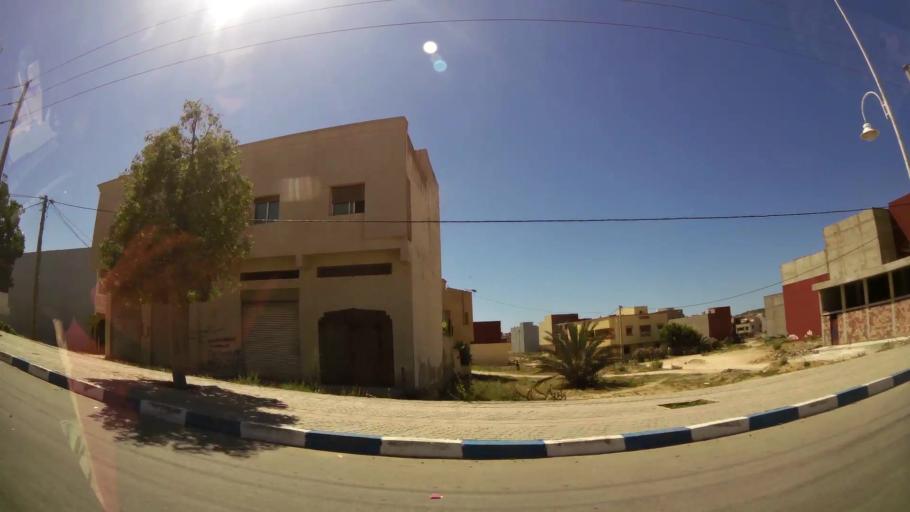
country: MA
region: Oriental
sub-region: Berkane-Taourirt
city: Madagh
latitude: 35.1349
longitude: -2.4243
